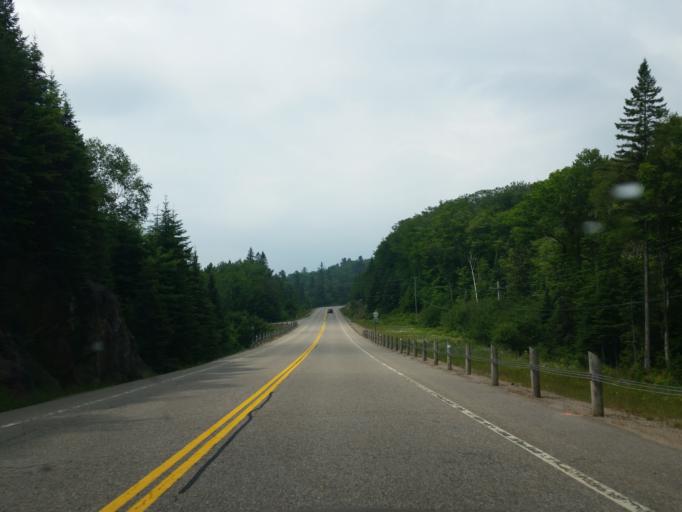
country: CA
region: Ontario
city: Huntsville
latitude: 45.5660
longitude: -78.5400
